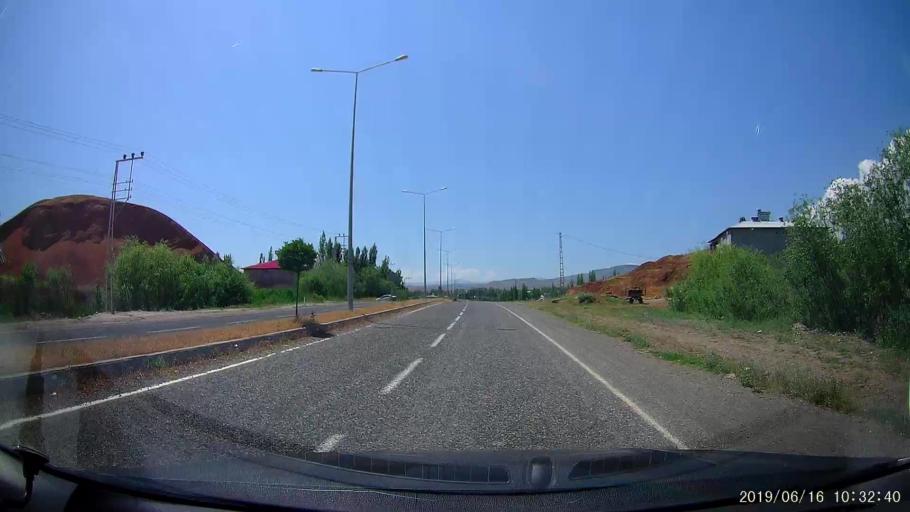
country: TR
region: Igdir
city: Tuzluca
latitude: 40.0483
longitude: 43.6540
